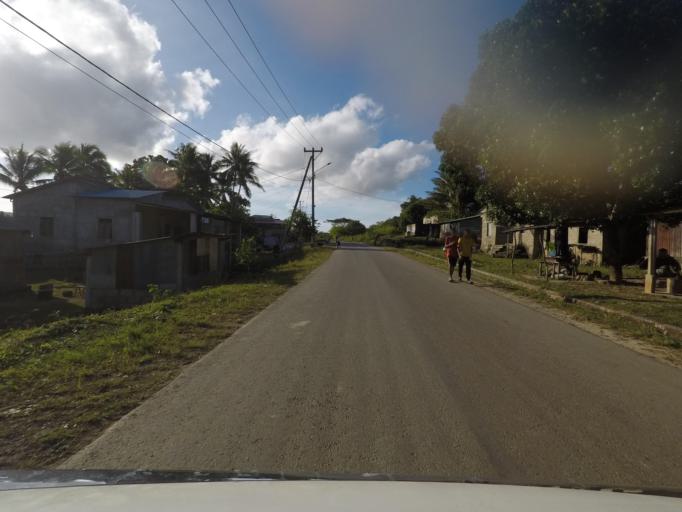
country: TL
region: Lautem
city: Lospalos
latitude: -8.4373
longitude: 127.0051
